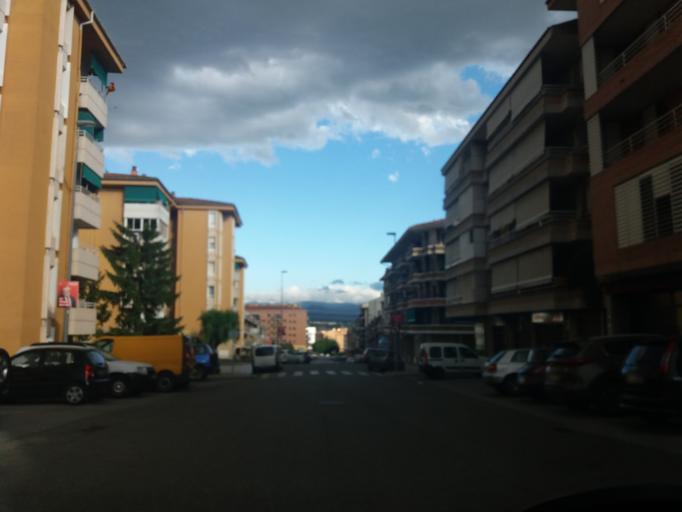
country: ES
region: Catalonia
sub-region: Provincia de Barcelona
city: Manresa
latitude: 41.7402
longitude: 1.8340
